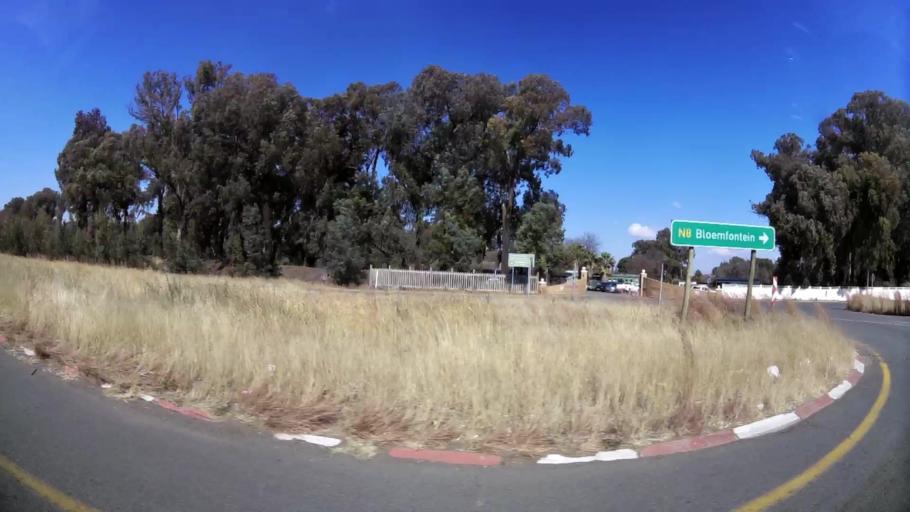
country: ZA
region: Orange Free State
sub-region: Mangaung Metropolitan Municipality
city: Bloemfontein
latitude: -29.1161
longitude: 26.2497
